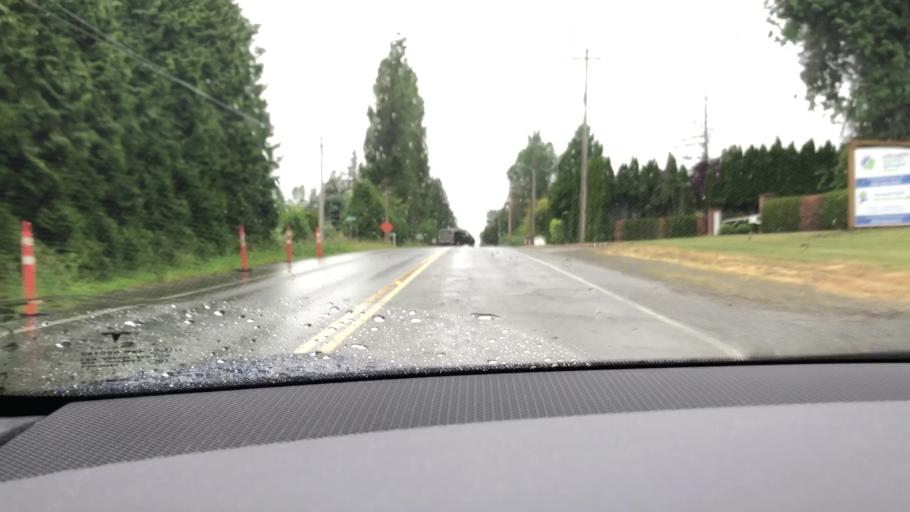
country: CA
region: British Columbia
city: Langley
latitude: 49.1335
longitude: -122.6534
